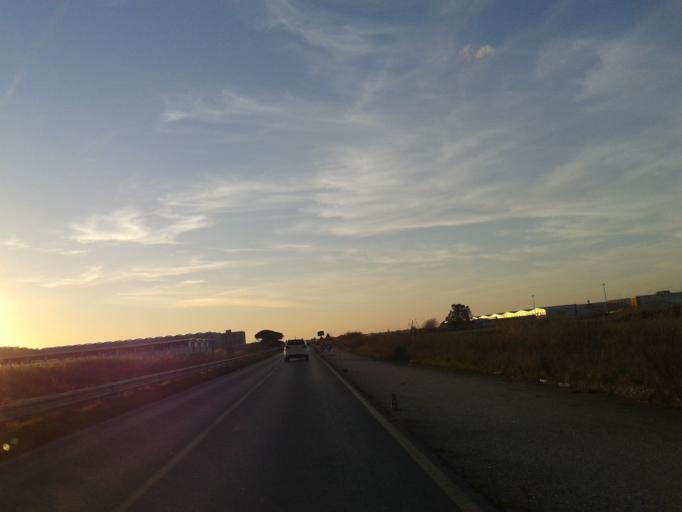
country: IT
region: Tuscany
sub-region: Provincia di Livorno
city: Guasticce
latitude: 43.5968
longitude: 10.3862
